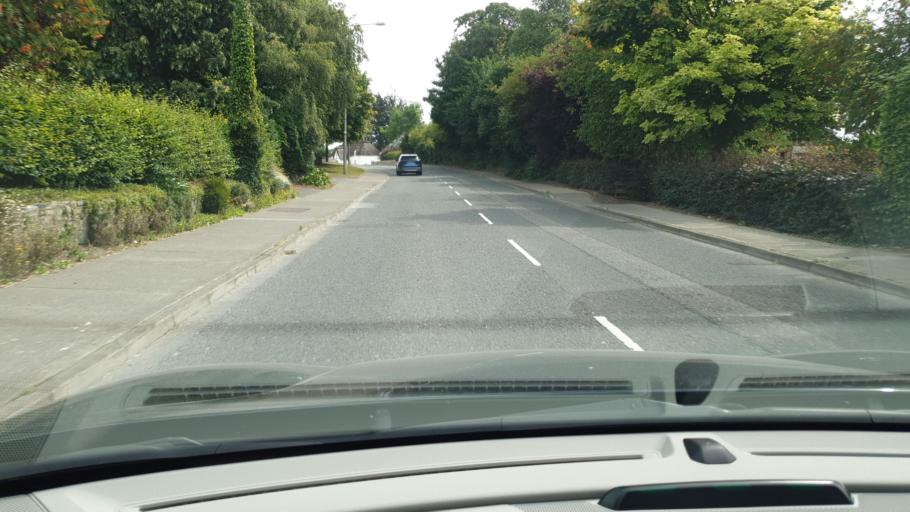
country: IE
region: Leinster
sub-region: An Mhi
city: Navan
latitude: 53.6517
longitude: -6.6711
